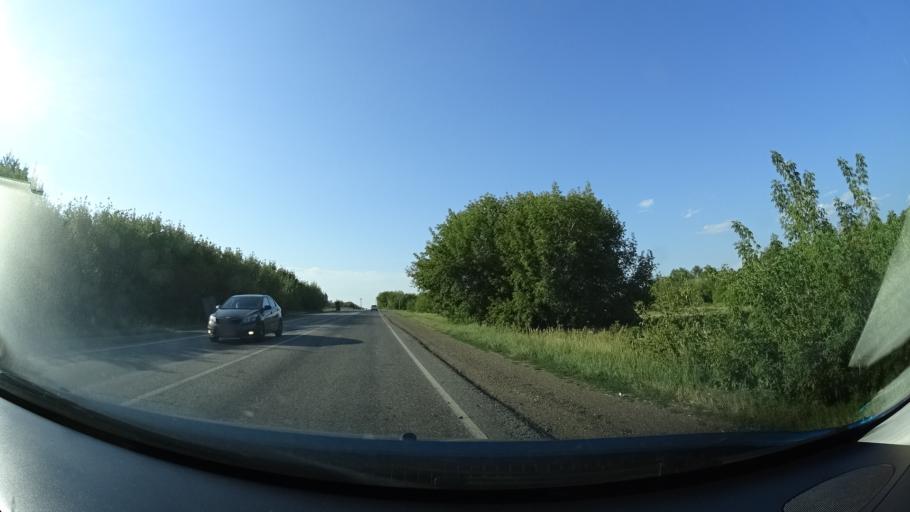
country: RU
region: Bashkortostan
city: Salavat
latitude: 53.4498
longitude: 55.9209
